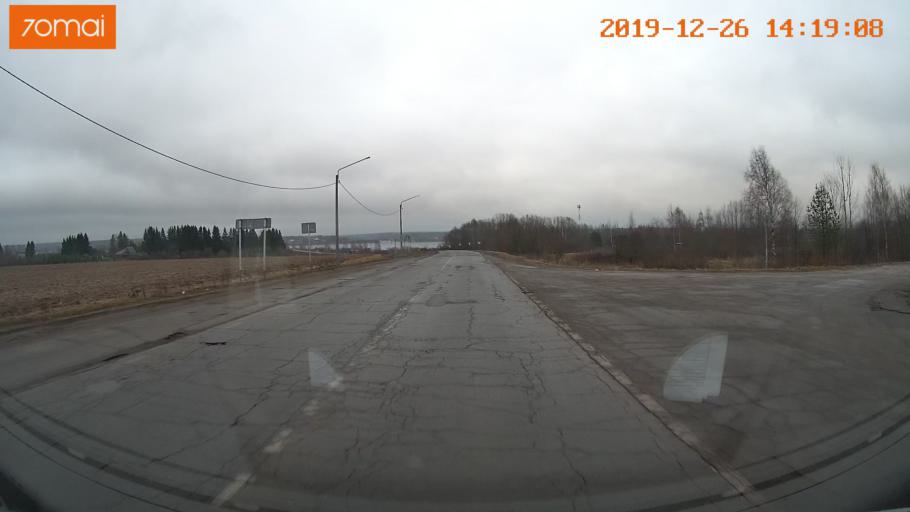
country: RU
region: Jaroslavl
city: Poshekhon'ye
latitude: 58.5116
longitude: 39.1095
